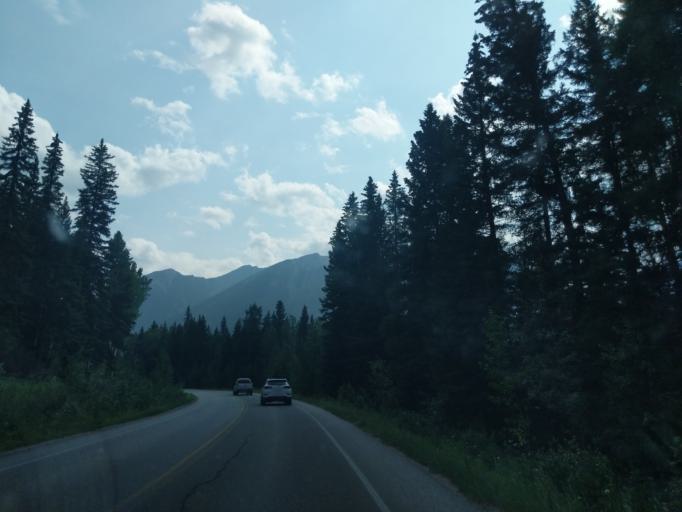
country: CA
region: Alberta
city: Banff
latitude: 51.1838
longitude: -115.7239
